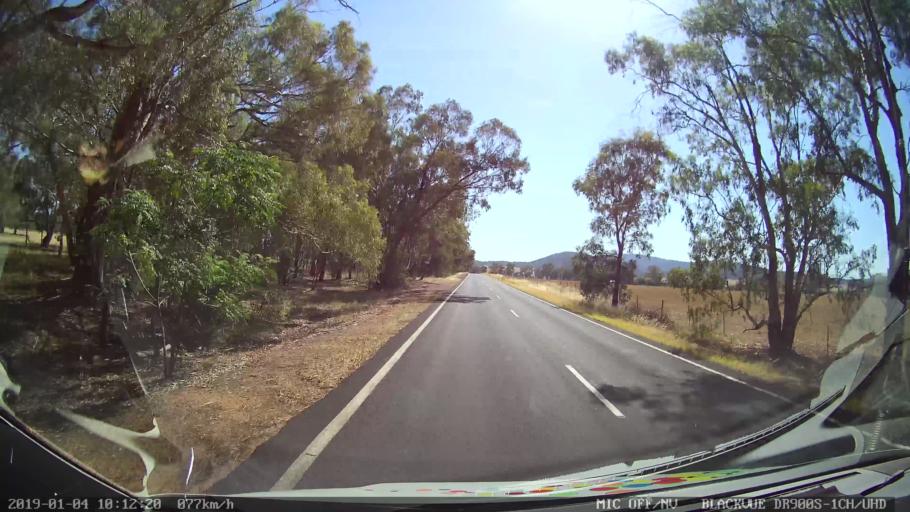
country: AU
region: New South Wales
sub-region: Cabonne
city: Canowindra
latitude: -33.4131
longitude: 148.3936
